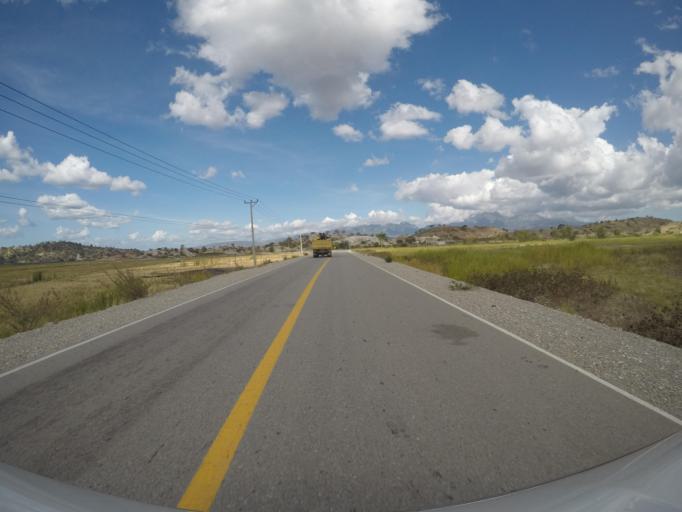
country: TL
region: Baucau
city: Baucau
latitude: -8.4726
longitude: 126.4999
